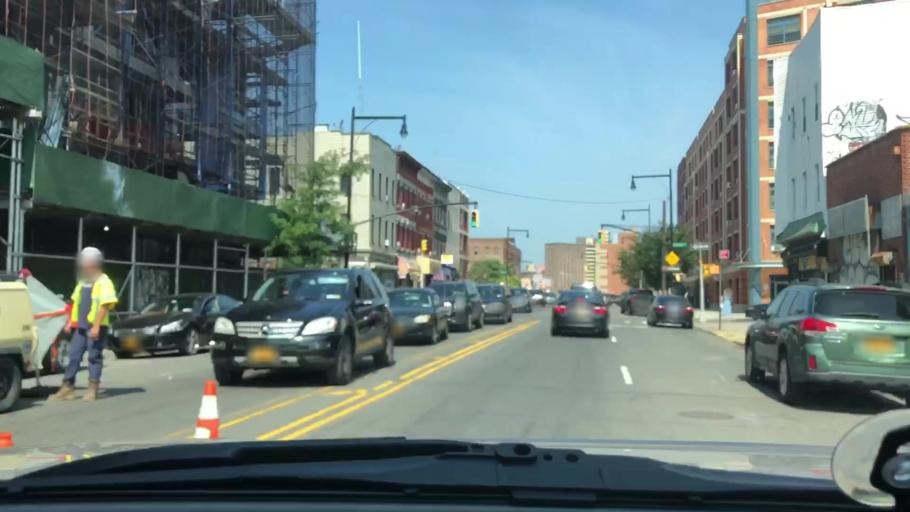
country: US
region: New York
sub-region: Queens County
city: Long Island City
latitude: 40.6985
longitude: -73.9343
